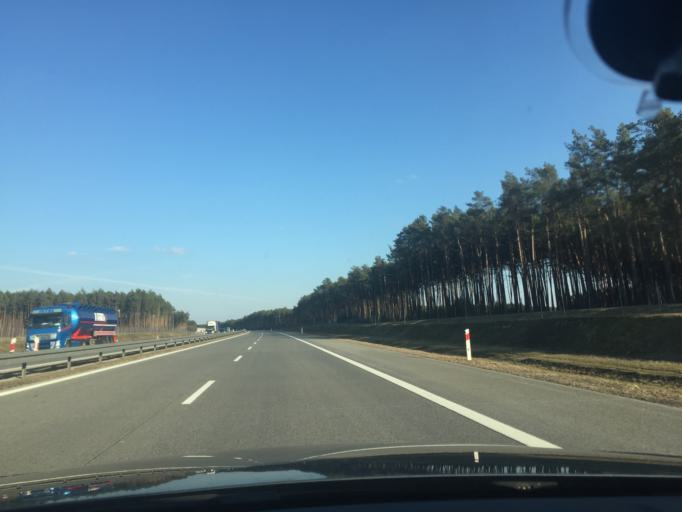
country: PL
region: Lubusz
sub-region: Powiat swiebodzinski
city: Szczaniec
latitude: 52.2967
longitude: 15.7154
